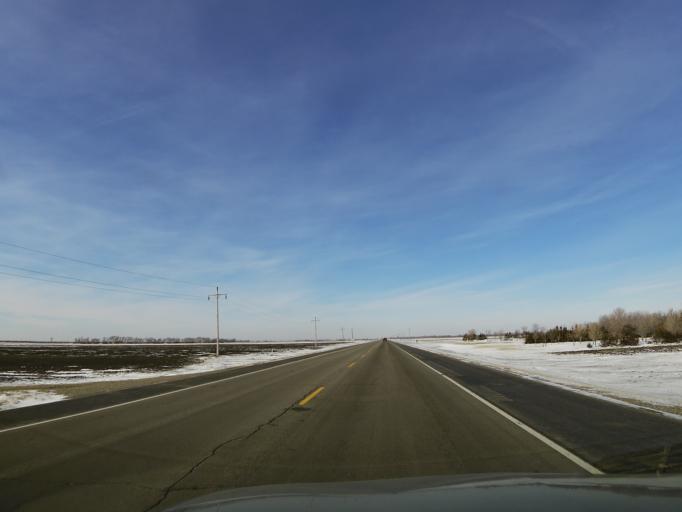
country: US
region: North Dakota
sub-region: Walsh County
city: Grafton
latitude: 48.4122
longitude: -97.2704
